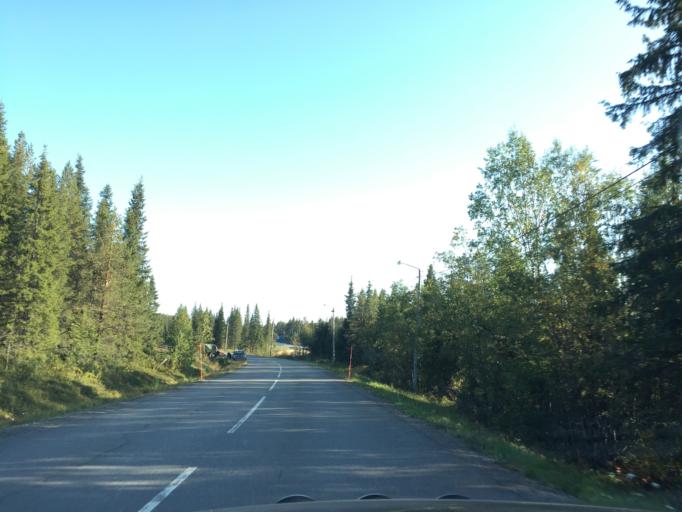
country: SE
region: Norrbotten
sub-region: Gallivare Kommun
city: Malmberget
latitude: 67.6418
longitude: 21.0602
